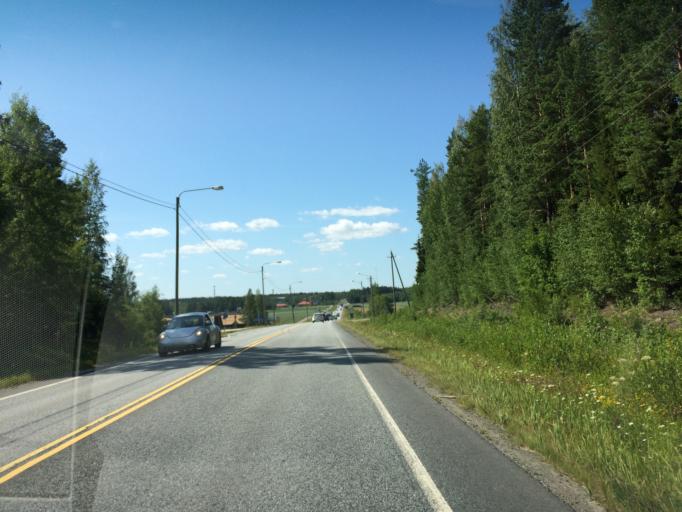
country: FI
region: Pirkanmaa
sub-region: Lounais-Pirkanmaa
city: Kiikoinen
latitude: 61.4768
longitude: 22.5774
